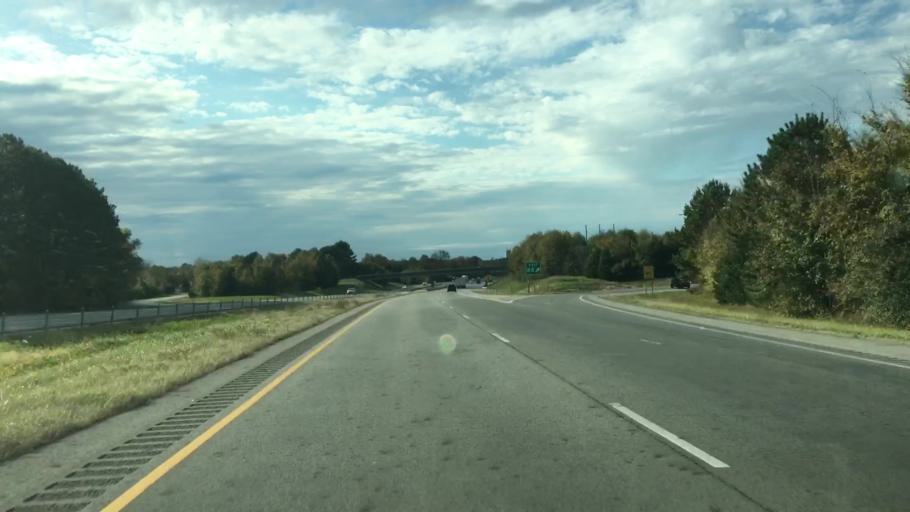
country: US
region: Arkansas
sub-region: Pope County
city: Pottsville
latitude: 35.2489
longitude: -93.0312
